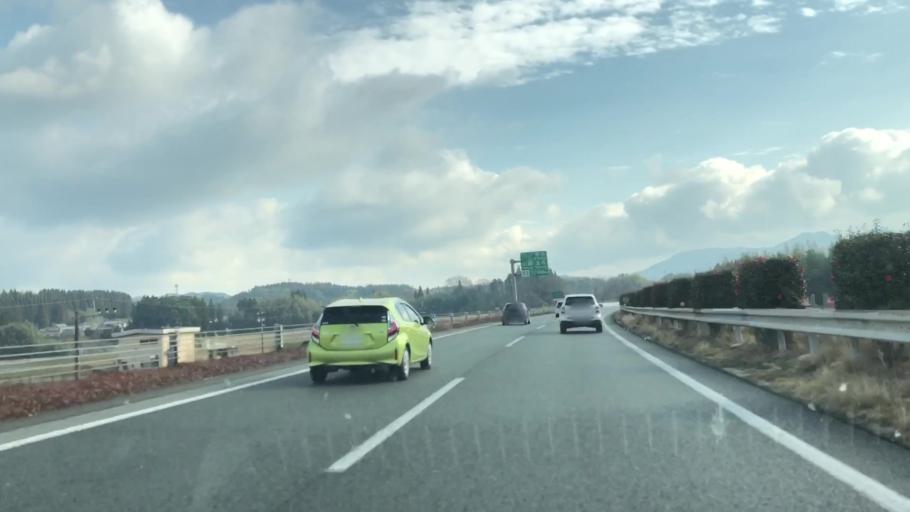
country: JP
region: Kumamoto
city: Tamana
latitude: 32.9940
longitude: 130.6002
